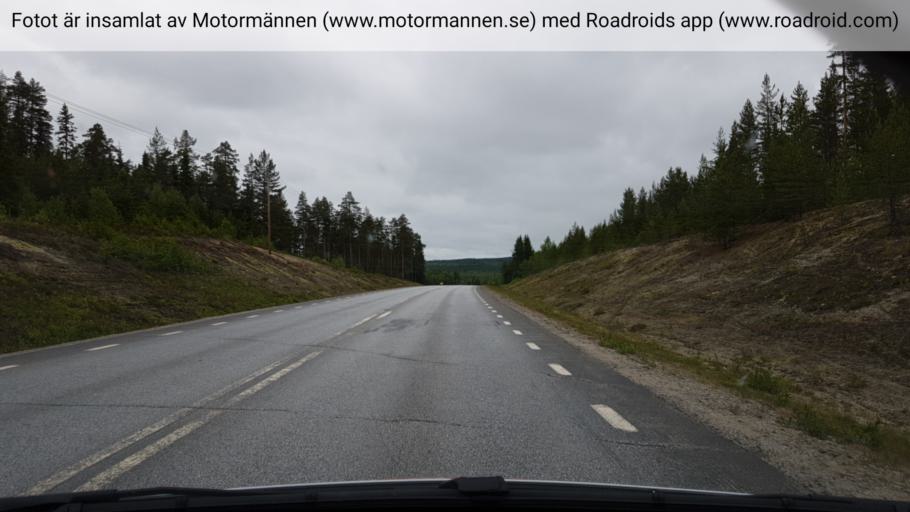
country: SE
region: Vaesterbotten
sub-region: Vannas Kommun
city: Vaennaes
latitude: 64.0344
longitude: 19.6906
